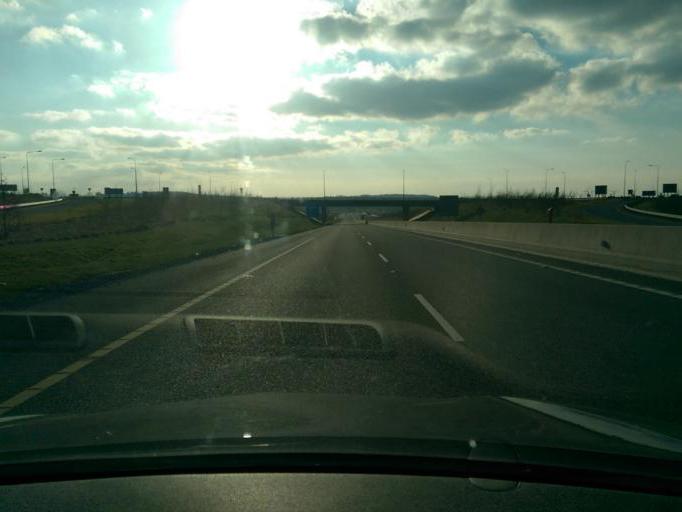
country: IE
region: Leinster
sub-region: Laois
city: Rathdowney
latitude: 52.9238
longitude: -7.6264
